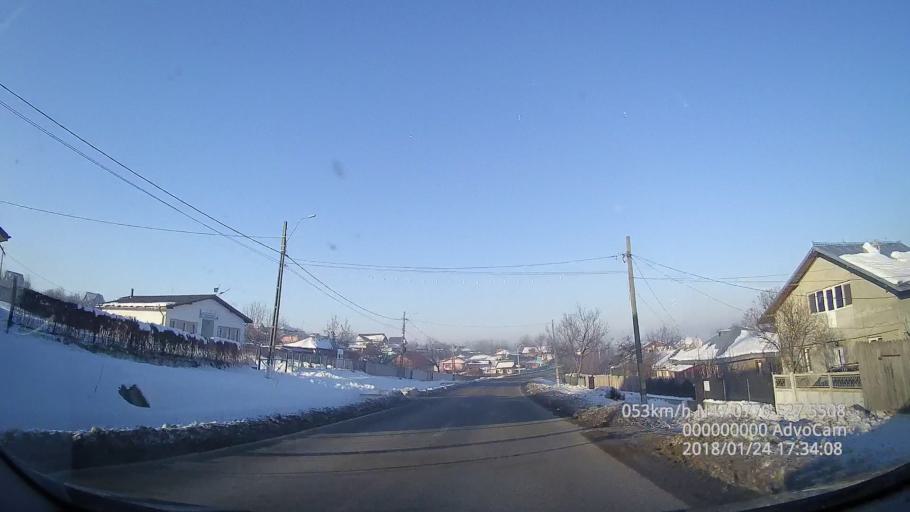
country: RO
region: Iasi
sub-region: Comuna Ciurea
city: Dumbrava
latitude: 47.0780
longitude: 27.5508
